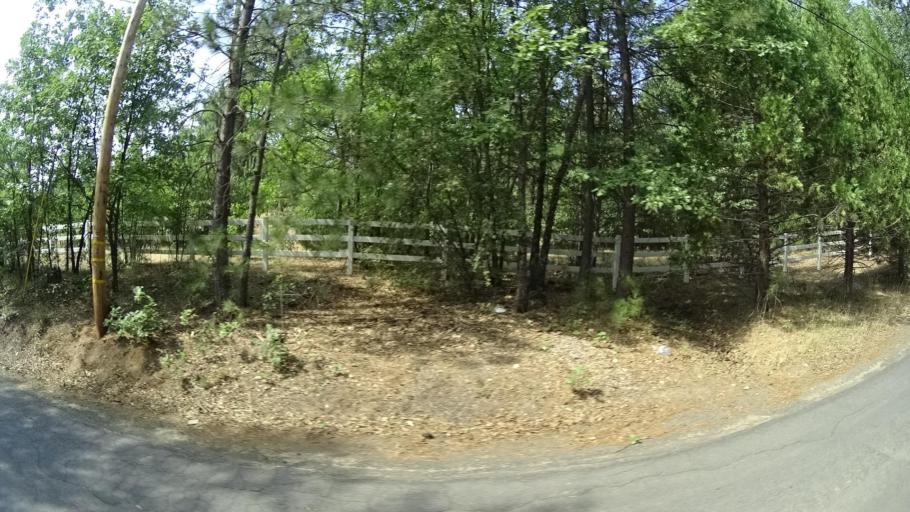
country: US
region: California
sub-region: Tuolumne County
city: Tuolumne City
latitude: 37.7722
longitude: -120.1793
